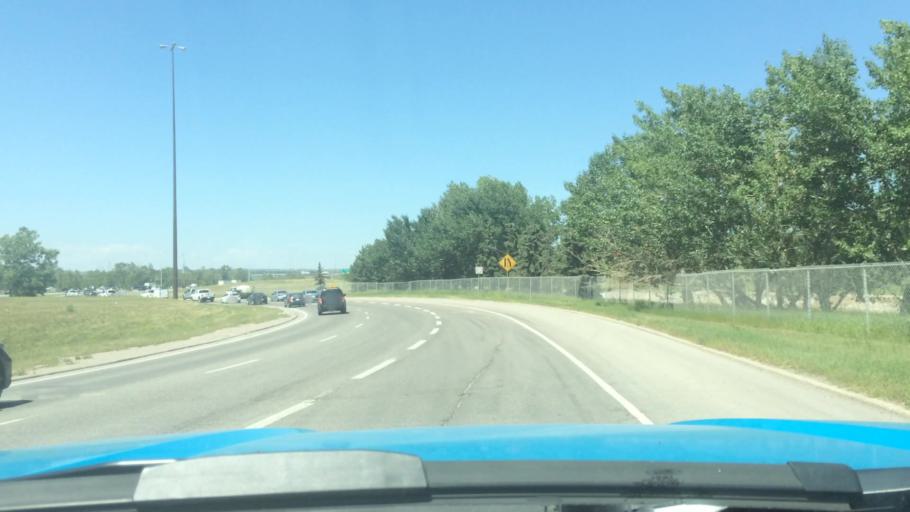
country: CA
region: Alberta
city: Calgary
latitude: 51.0376
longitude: -114.0027
